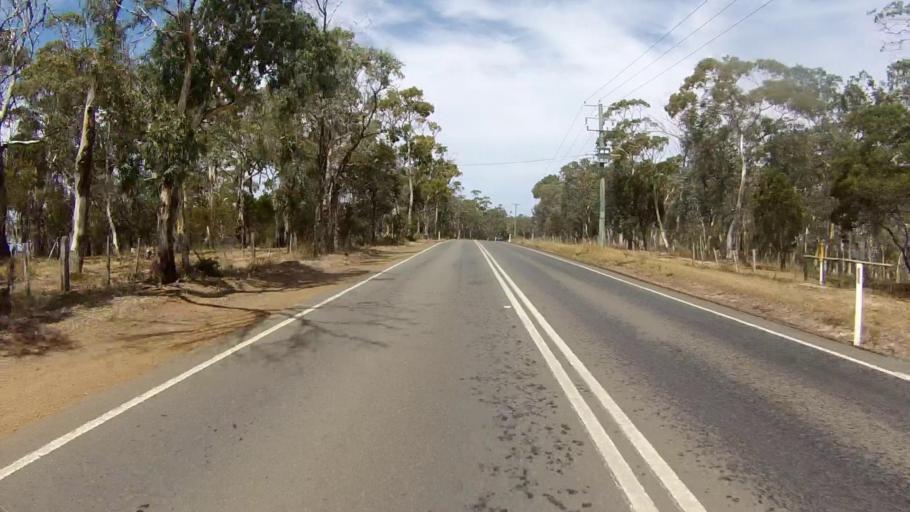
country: AU
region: Tasmania
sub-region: Clarence
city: Sandford
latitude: -42.9724
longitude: 147.5037
